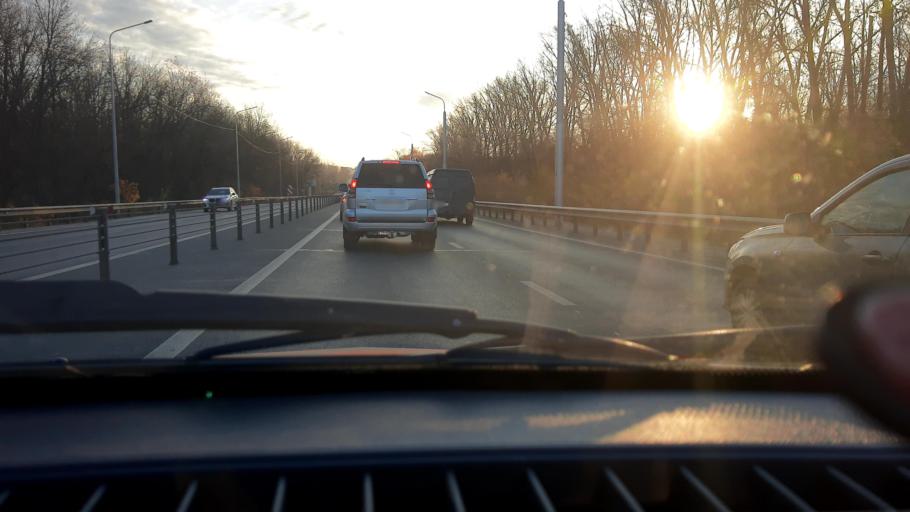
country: RU
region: Bashkortostan
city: Ufa
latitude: 54.7001
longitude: 55.9249
